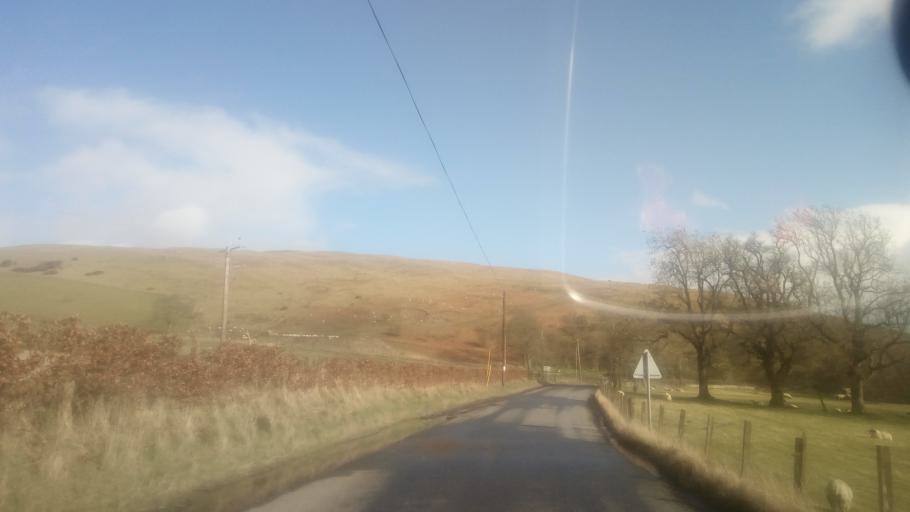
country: GB
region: Scotland
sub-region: The Scottish Borders
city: Hawick
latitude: 55.4170
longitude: -2.8552
